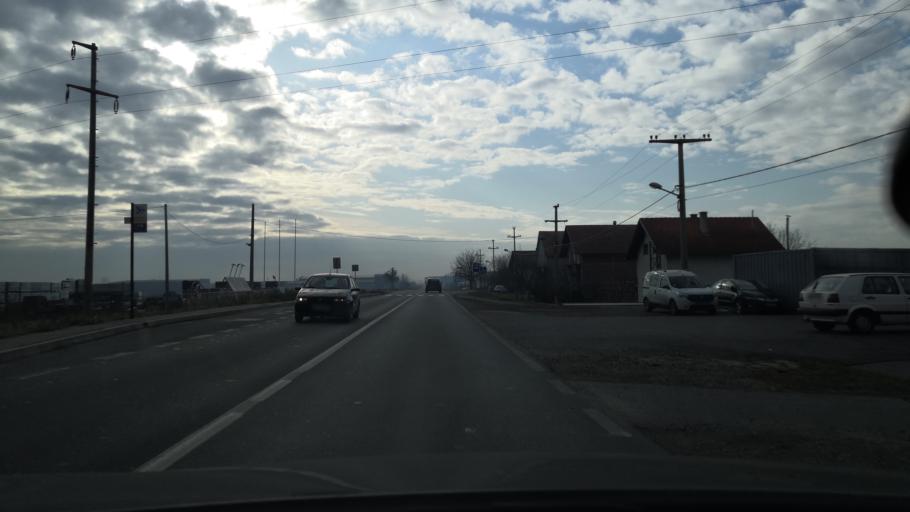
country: RS
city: Ugrinovci
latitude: 44.8610
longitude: 20.2048
